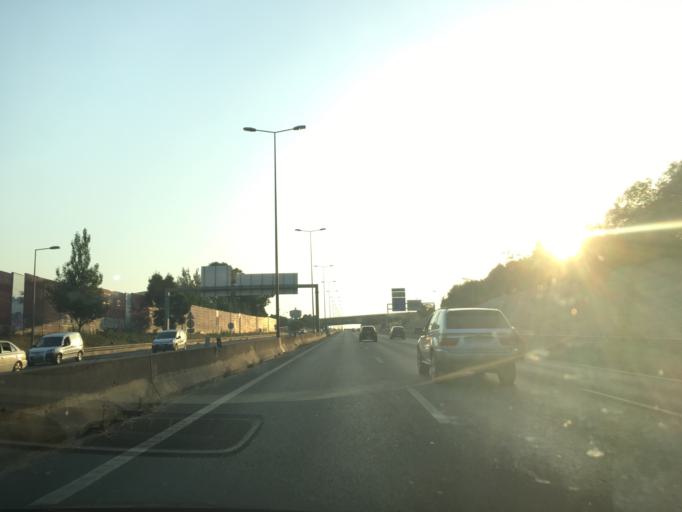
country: PT
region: Lisbon
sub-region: Sintra
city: Queluz
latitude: 38.7478
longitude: -9.2672
